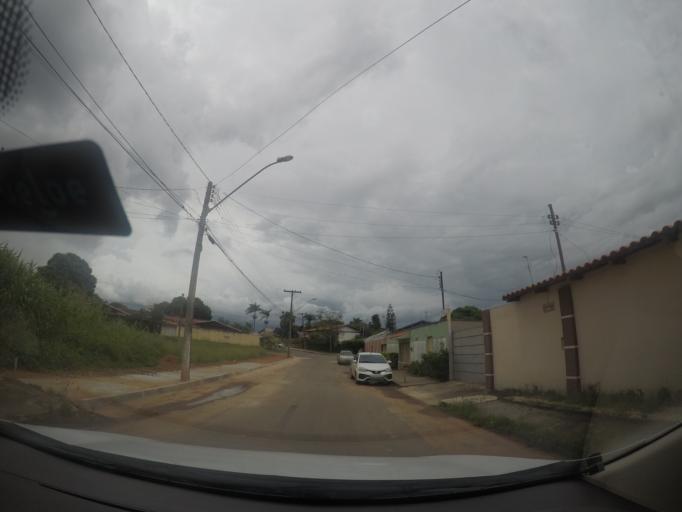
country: BR
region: Goias
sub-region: Goiania
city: Goiania
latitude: -16.6541
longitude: -49.2325
